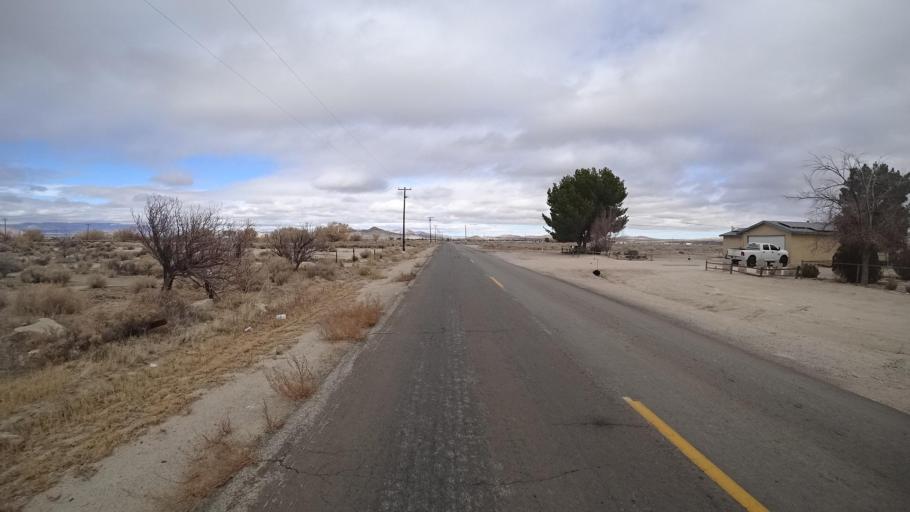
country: US
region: California
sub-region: Kern County
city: Rosamond
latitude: 34.8292
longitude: -118.1670
